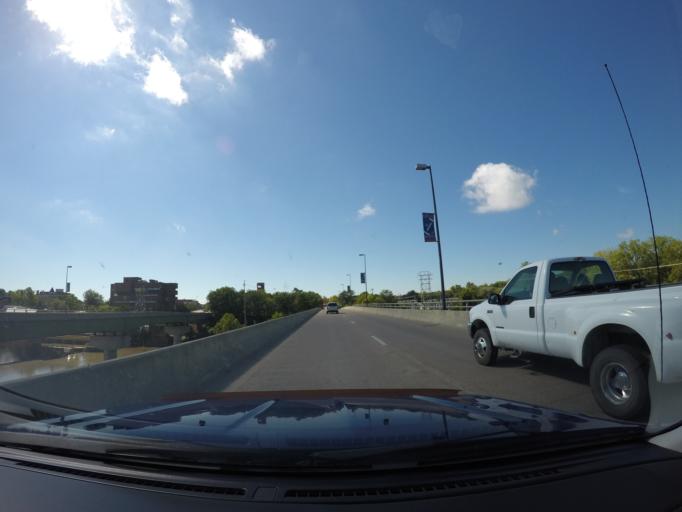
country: US
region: Kansas
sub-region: Douglas County
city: Lawrence
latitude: 38.9751
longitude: -95.2363
